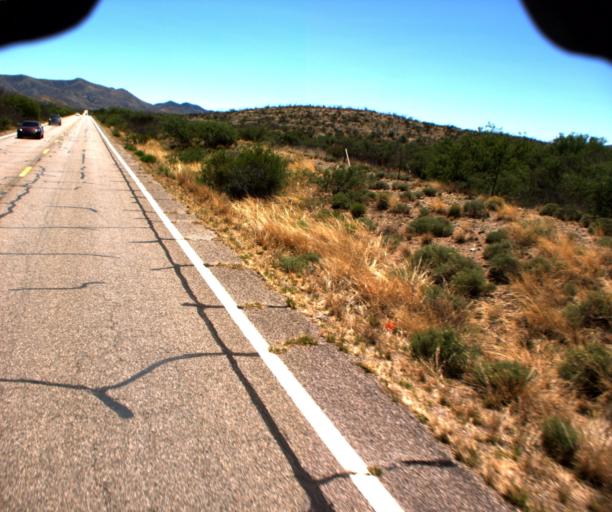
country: US
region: Arizona
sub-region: Pima County
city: Vail
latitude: 31.9515
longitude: -110.6673
